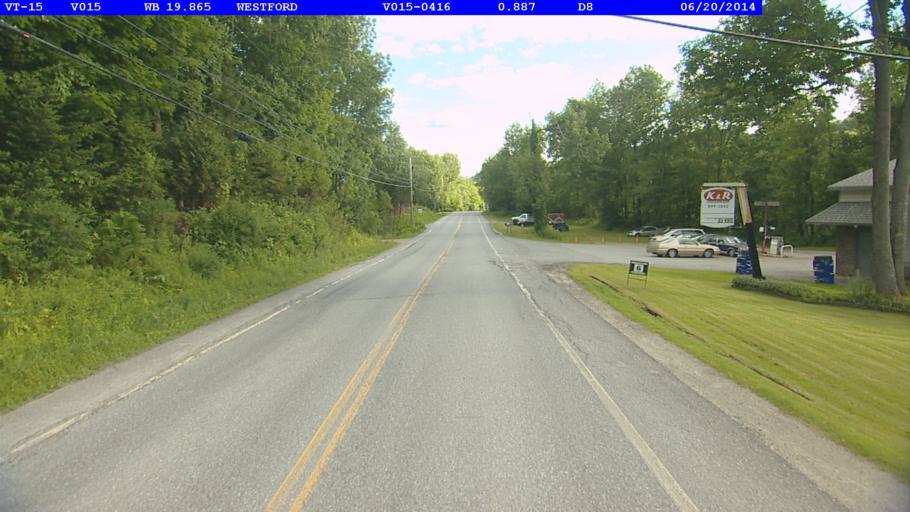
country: US
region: Vermont
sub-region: Chittenden County
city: Jericho
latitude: 44.6064
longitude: -72.9320
